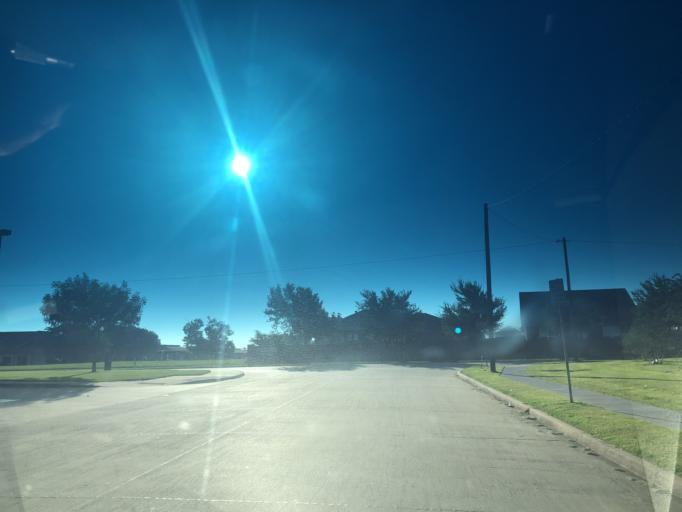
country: US
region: Texas
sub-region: Dallas County
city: Grand Prairie
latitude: 32.7082
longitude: -97.0204
